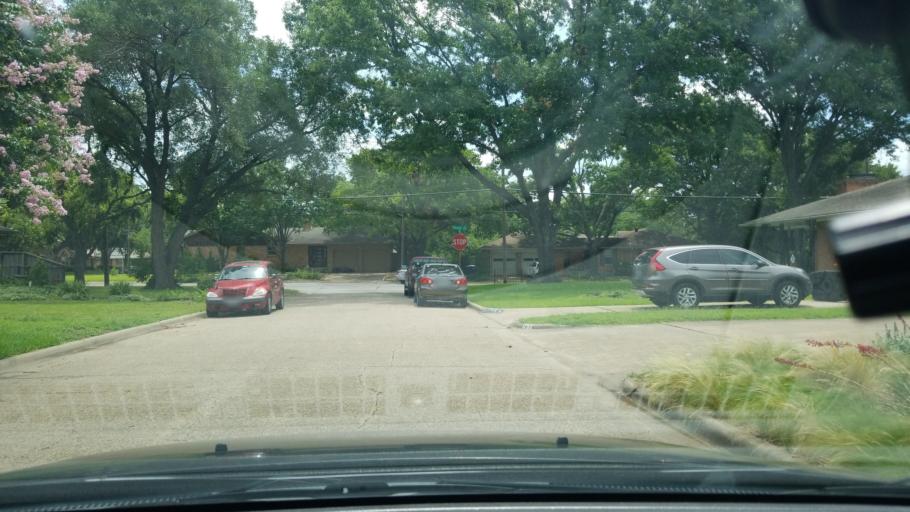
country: US
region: Texas
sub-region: Dallas County
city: Garland
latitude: 32.8252
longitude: -96.6845
